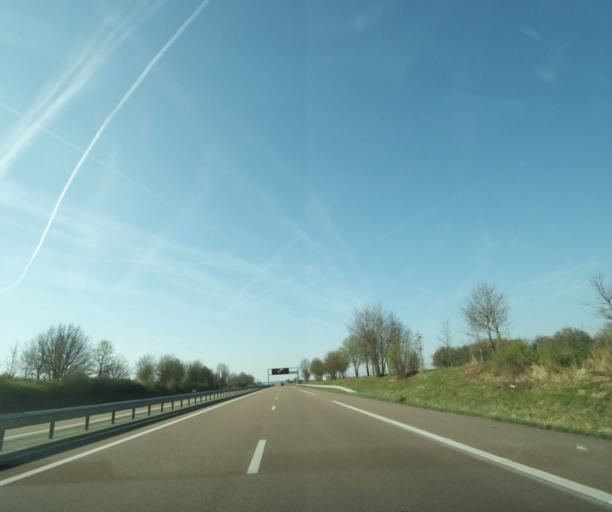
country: FR
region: Ile-de-France
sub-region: Departement de Seine-et-Marne
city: Souppes-sur-Loing
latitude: 48.2030
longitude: 2.7719
